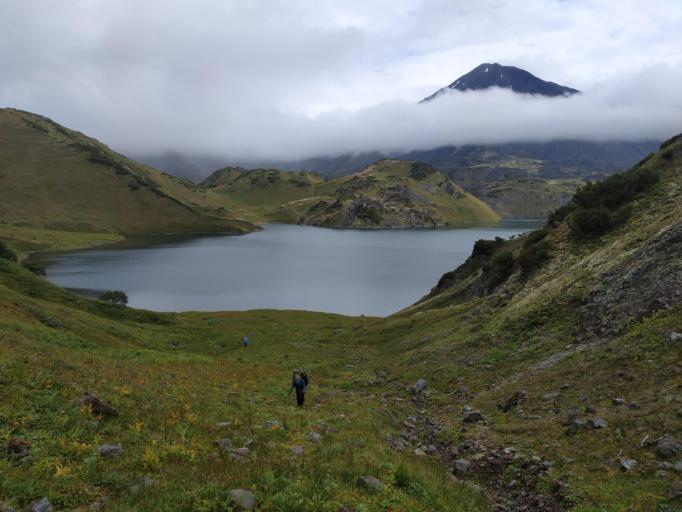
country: RU
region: Kamtsjatka
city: Yelizovo
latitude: 53.8721
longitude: 158.0268
